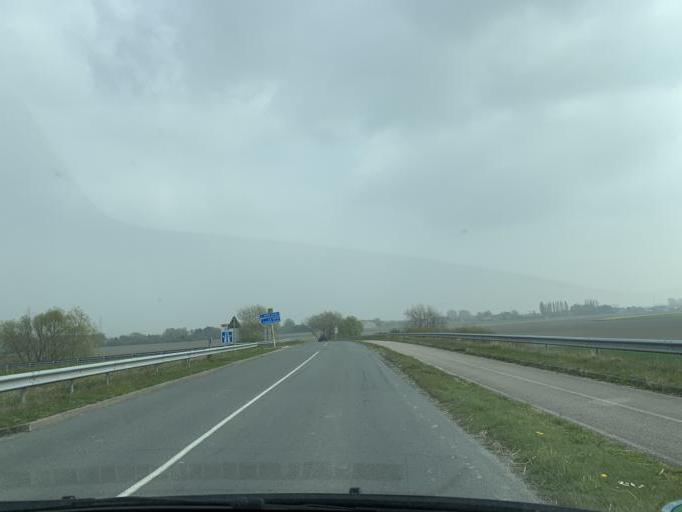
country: FR
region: Nord-Pas-de-Calais
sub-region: Departement du Nord
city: Leffrinckoucke
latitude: 51.0388
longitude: 2.4532
